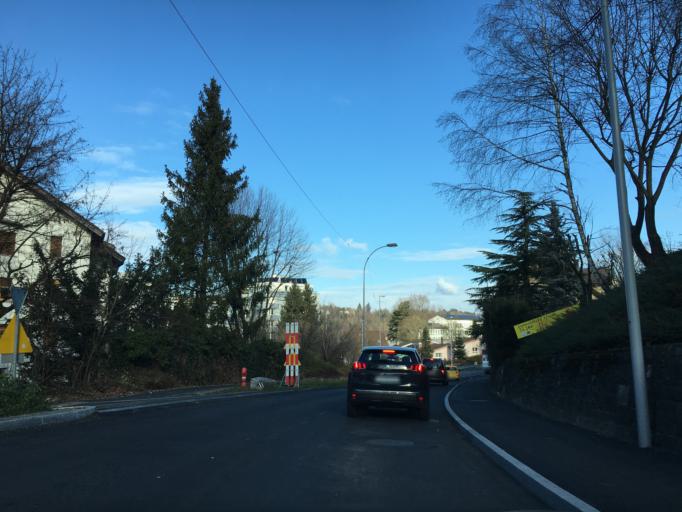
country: CH
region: Lucerne
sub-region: Lucerne-Land District
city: Ebikon
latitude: 47.0761
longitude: 8.3375
